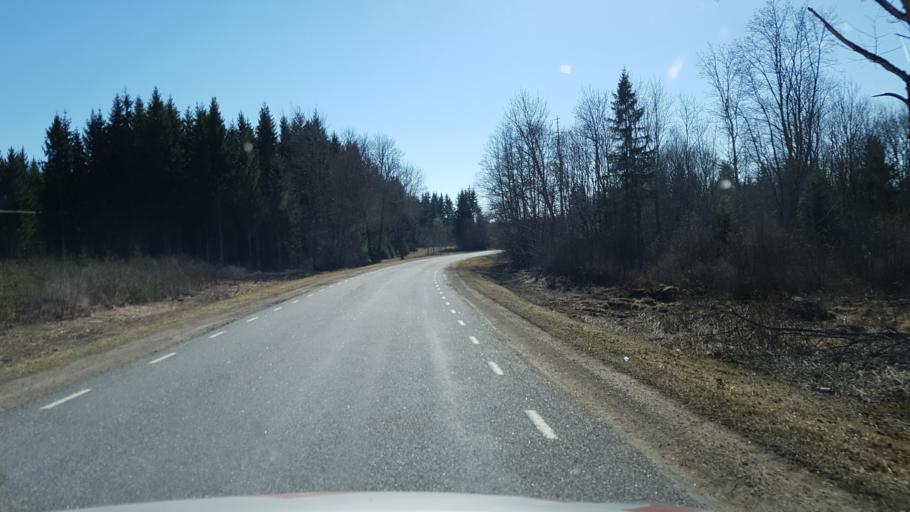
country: EE
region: Laeaene-Virumaa
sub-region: Tamsalu vald
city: Tamsalu
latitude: 59.0556
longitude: 26.1003
